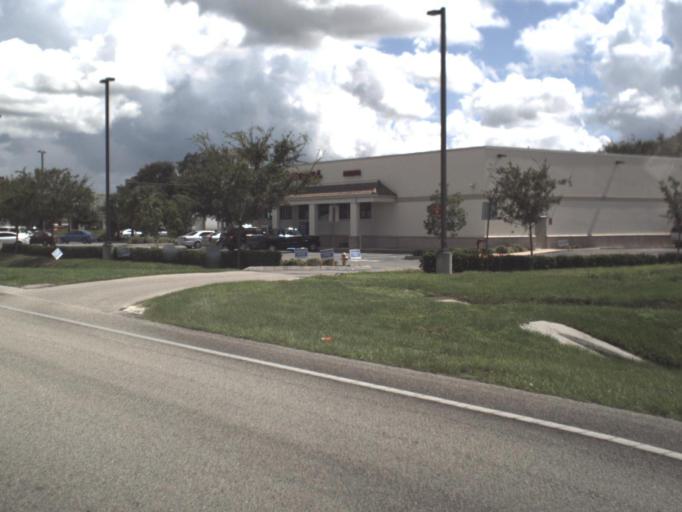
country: US
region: Florida
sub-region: DeSoto County
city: Arcadia
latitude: 27.2089
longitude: -81.8344
